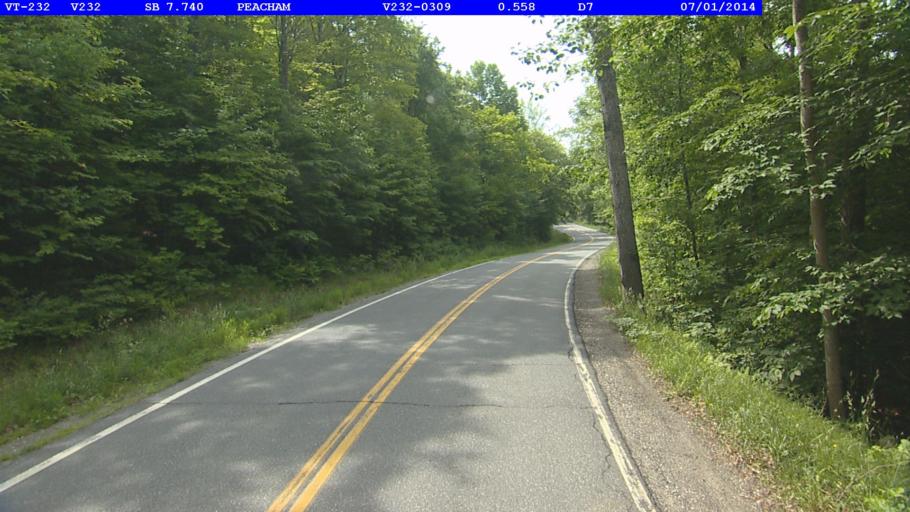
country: US
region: Vermont
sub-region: Caledonia County
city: Hardwick
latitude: 44.3036
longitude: -72.3020
